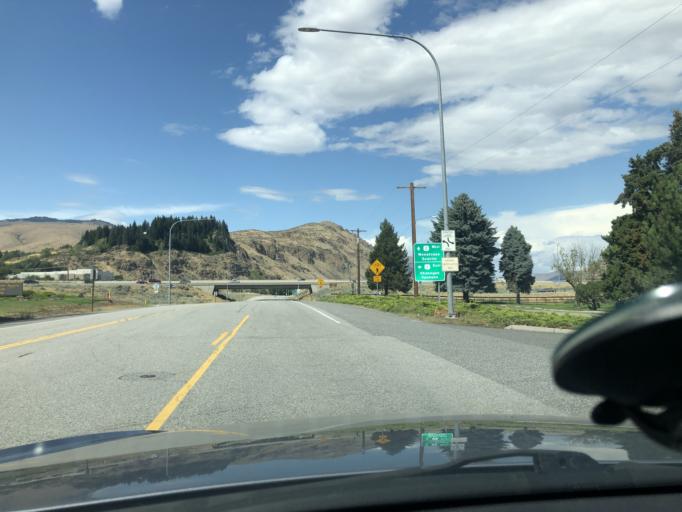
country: US
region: Washington
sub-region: Chelan County
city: Sunnyslope
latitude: 47.4697
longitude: -120.3247
